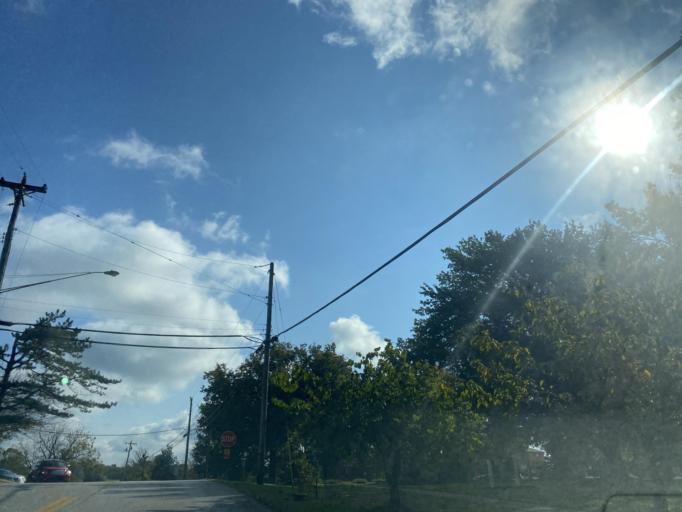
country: US
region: Kentucky
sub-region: Campbell County
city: Cold Spring
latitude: 39.0199
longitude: -84.4296
